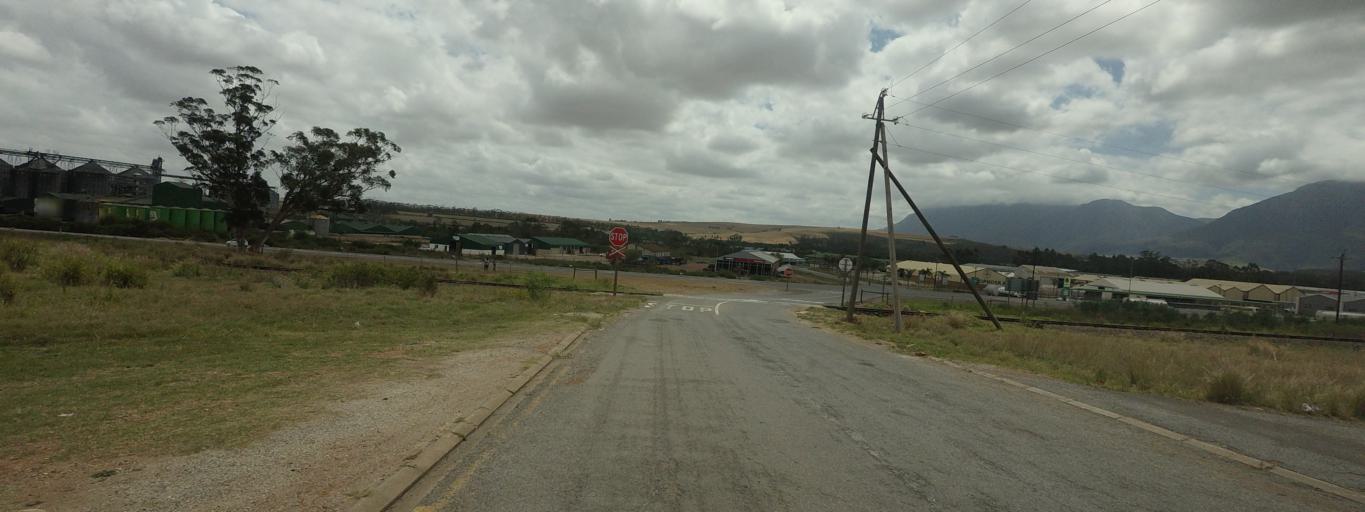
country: ZA
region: Western Cape
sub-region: Overberg District Municipality
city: Swellendam
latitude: -34.0526
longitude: 20.4281
